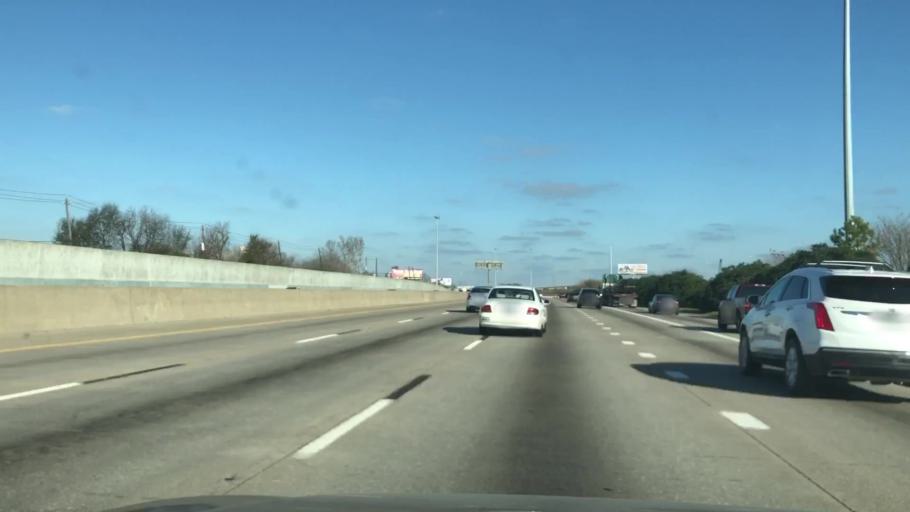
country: US
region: Texas
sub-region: Harris County
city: Jacinto City
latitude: 29.7630
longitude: -95.2652
